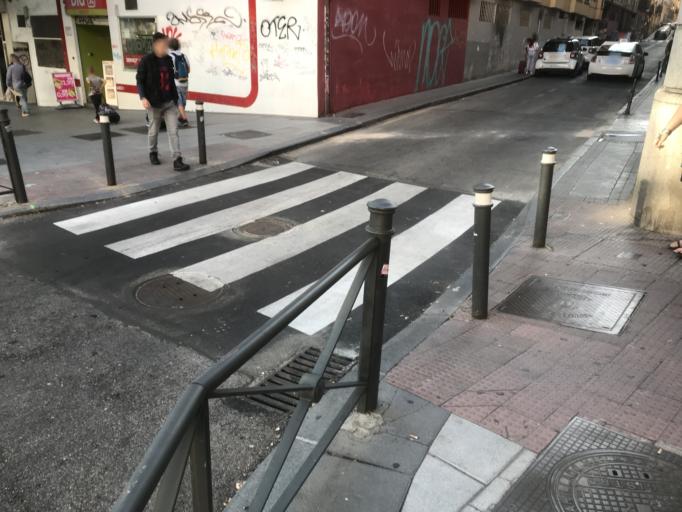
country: ES
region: Madrid
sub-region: Provincia de Madrid
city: Chamberi
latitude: 40.4284
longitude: -3.7062
